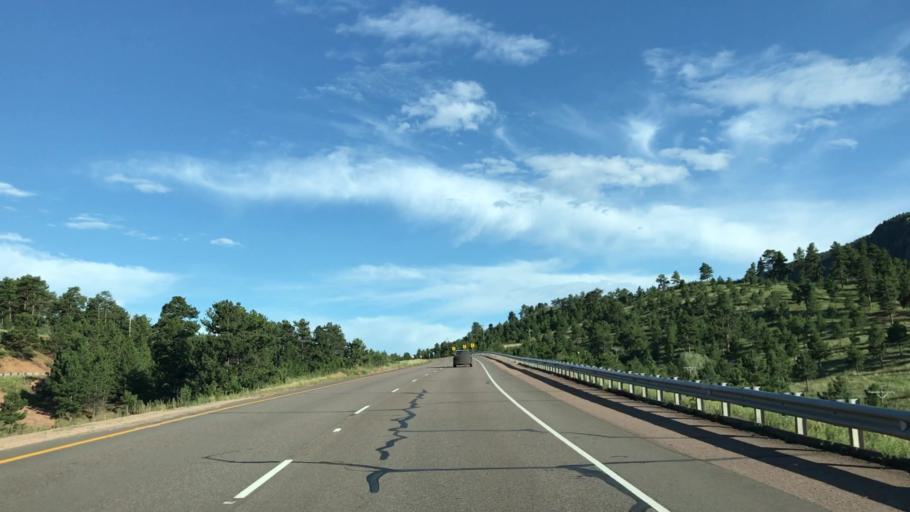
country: US
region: Colorado
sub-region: El Paso County
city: Cascade-Chipita Park
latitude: 38.9384
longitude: -105.0115
